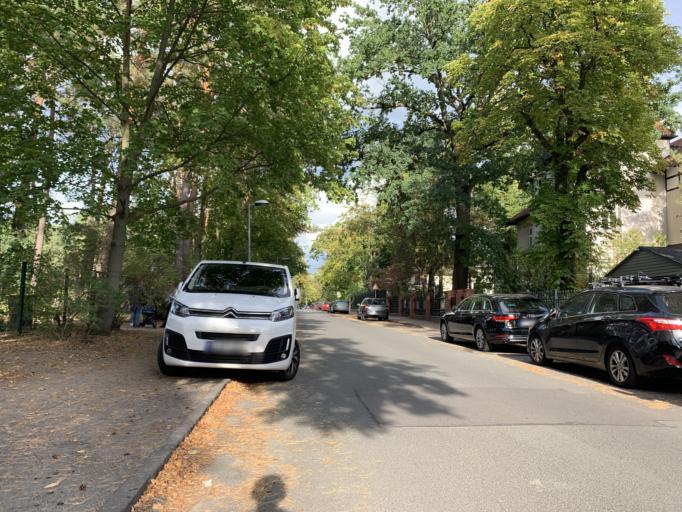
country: DE
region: Berlin
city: Wannsee
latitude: 52.4141
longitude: 13.1482
